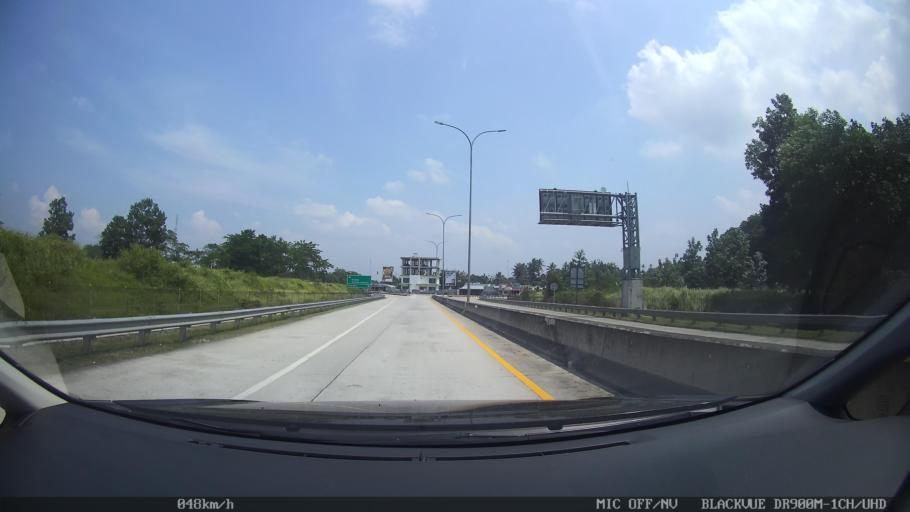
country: ID
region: Lampung
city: Kedaton
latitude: -5.3535
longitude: 105.3250
